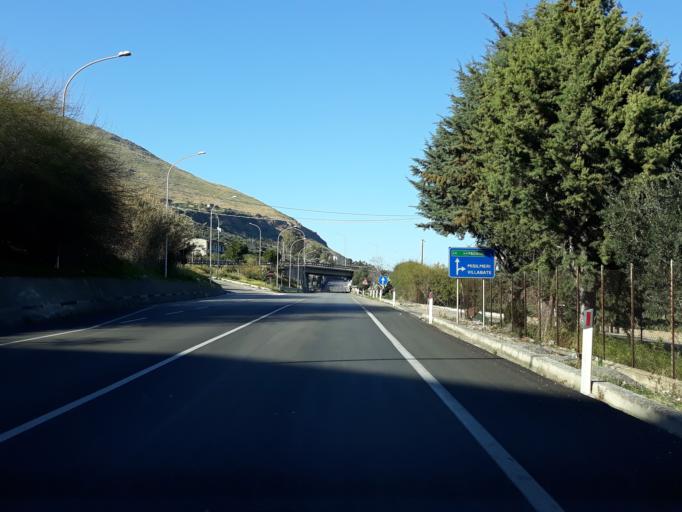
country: IT
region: Sicily
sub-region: Palermo
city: Misilmeri
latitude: 38.0415
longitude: 13.4609
